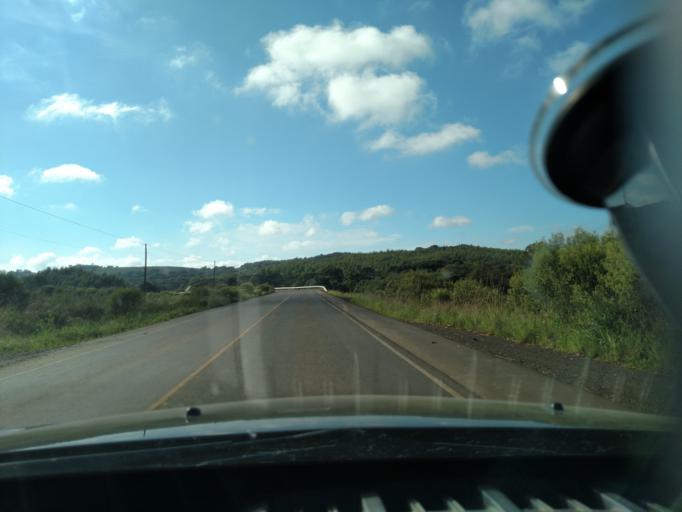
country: BR
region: Rio Grande do Sul
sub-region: Vacaria
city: Estrela
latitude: -27.9068
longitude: -50.7249
